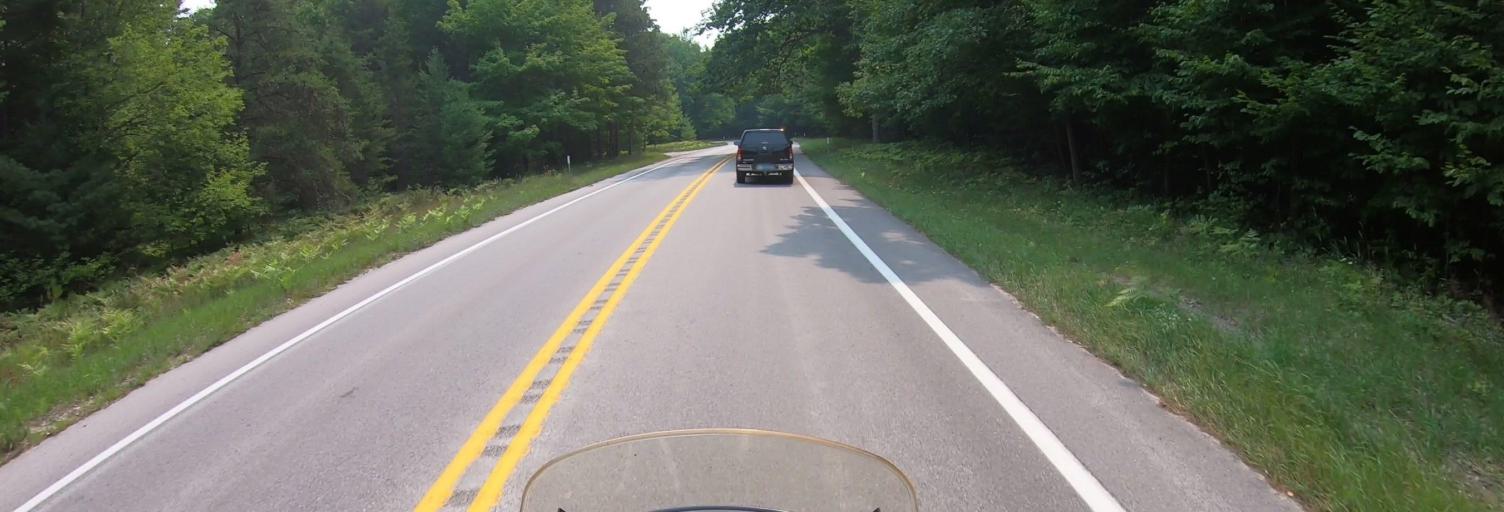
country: US
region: Michigan
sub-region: Leelanau County
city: Leland
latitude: 44.9342
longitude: -85.9110
